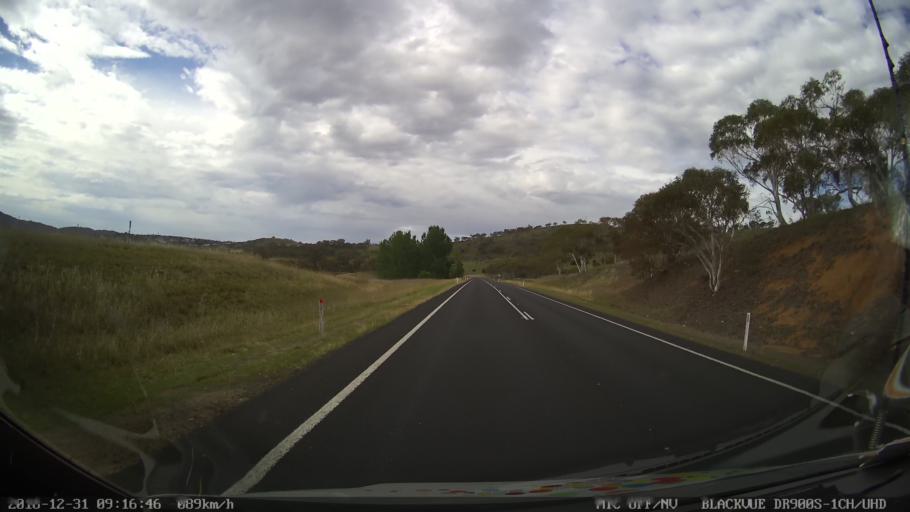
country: AU
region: New South Wales
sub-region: Snowy River
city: Jindabyne
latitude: -36.3998
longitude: 148.5971
